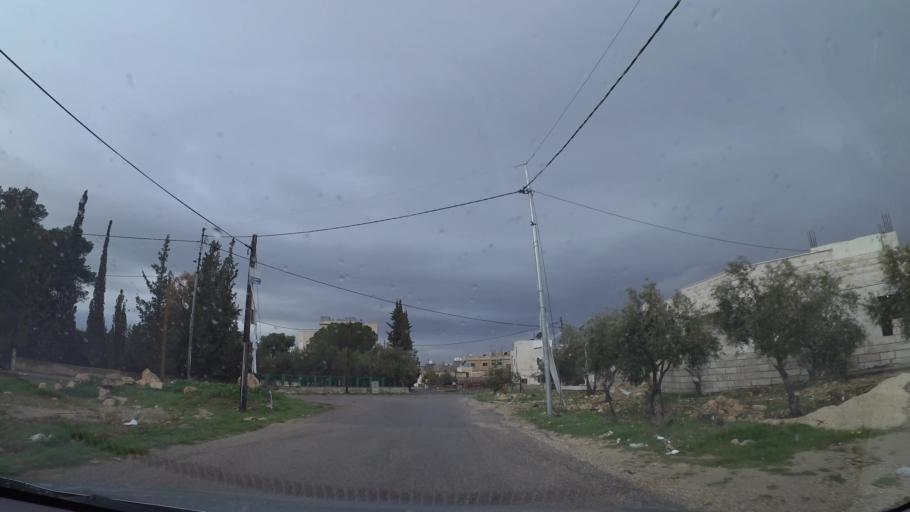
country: JO
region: Amman
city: Al Jubayhah
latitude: 32.0417
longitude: 35.8443
